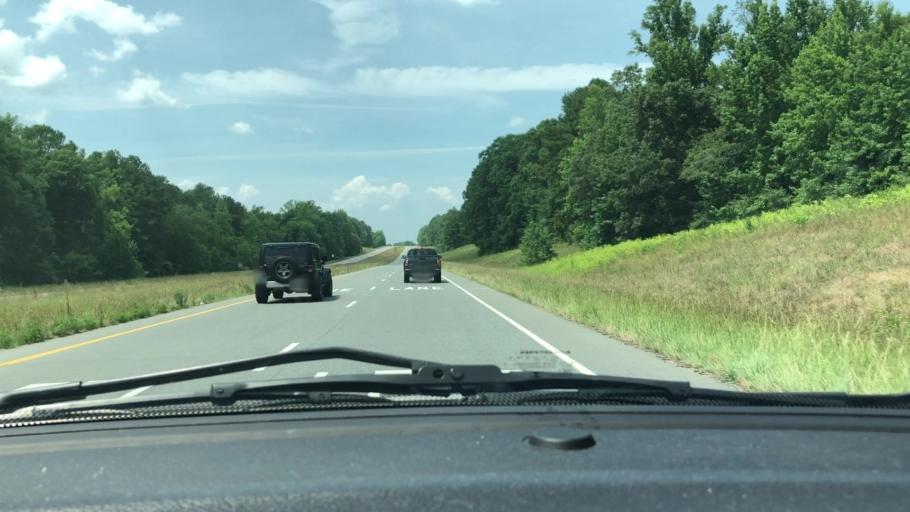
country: US
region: North Carolina
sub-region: Chatham County
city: Farmville
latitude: 35.5313
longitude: -79.2339
